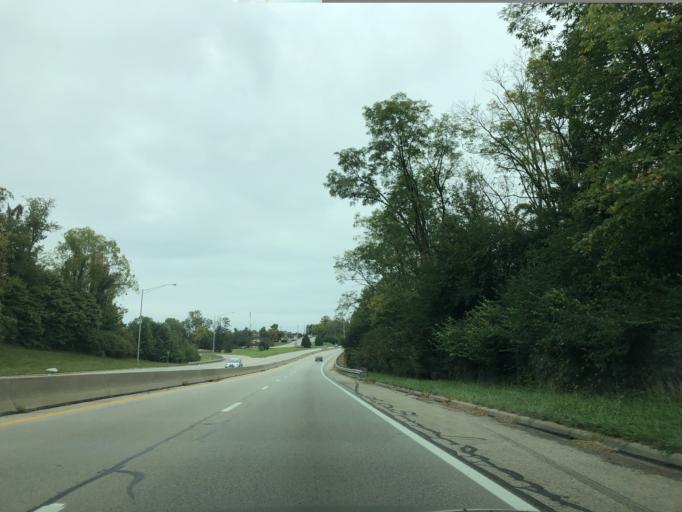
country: US
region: Ohio
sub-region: Hamilton County
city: Dillonvale
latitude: 39.2240
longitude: -84.4023
